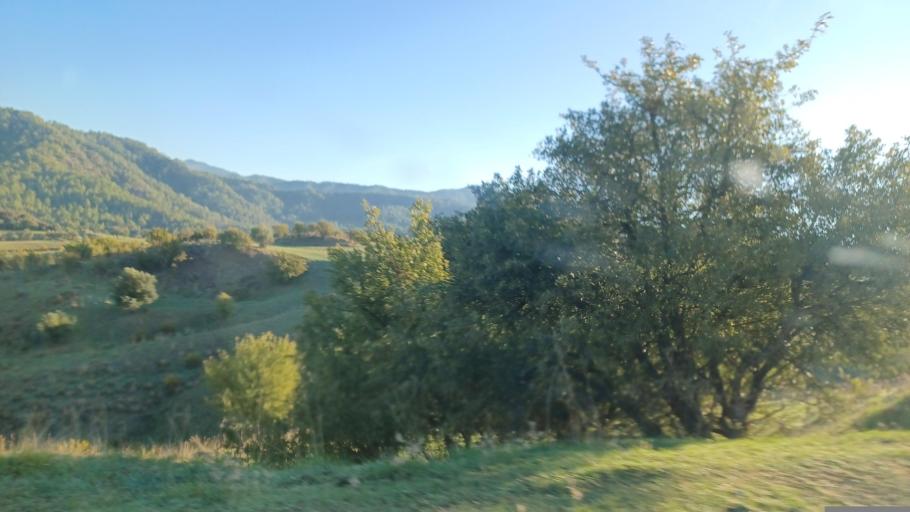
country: CY
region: Pafos
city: Polis
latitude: 34.9513
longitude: 32.5501
